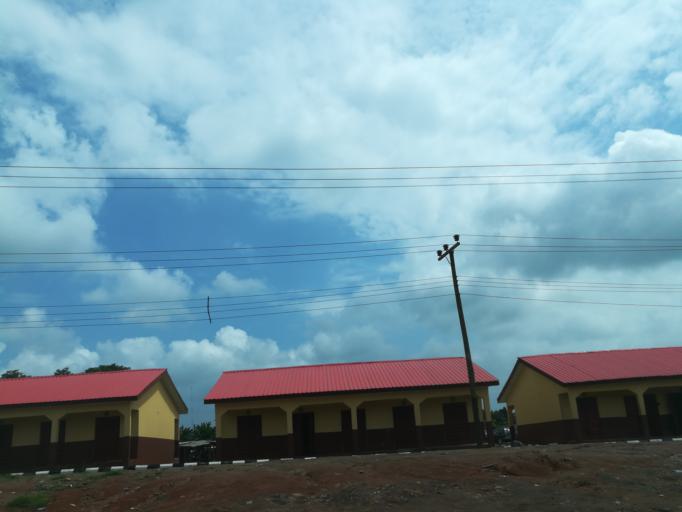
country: NG
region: Lagos
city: Ejirin
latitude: 6.6493
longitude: 3.7117
